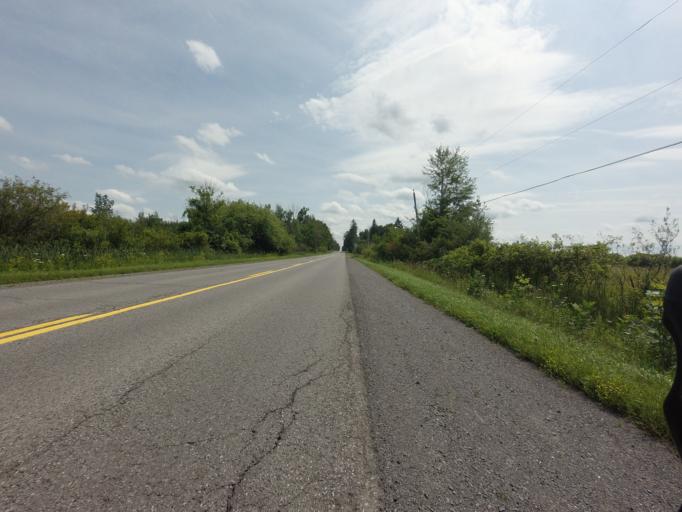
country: CA
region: Ontario
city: Ottawa
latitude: 45.2855
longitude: -75.6315
